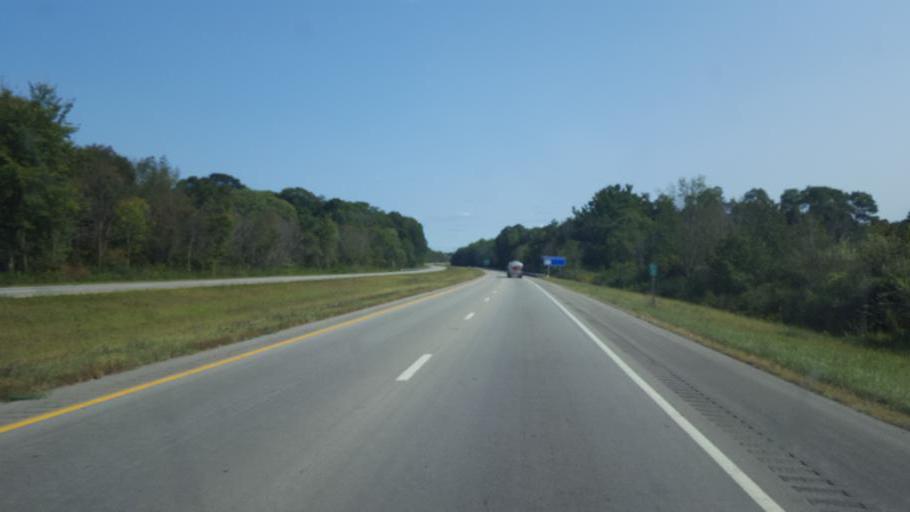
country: US
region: Ohio
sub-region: Stark County
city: Brewster
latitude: 40.7763
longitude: -81.5985
